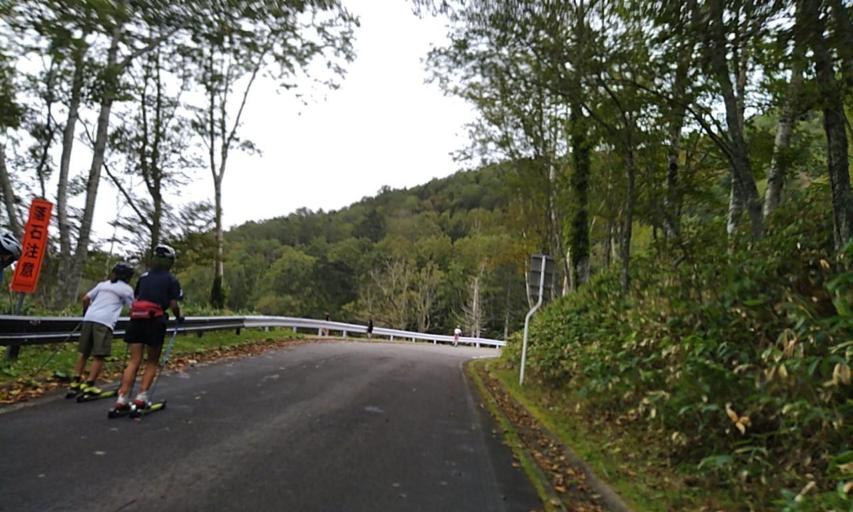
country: JP
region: Hokkaido
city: Bihoro
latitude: 43.5801
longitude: 144.2342
